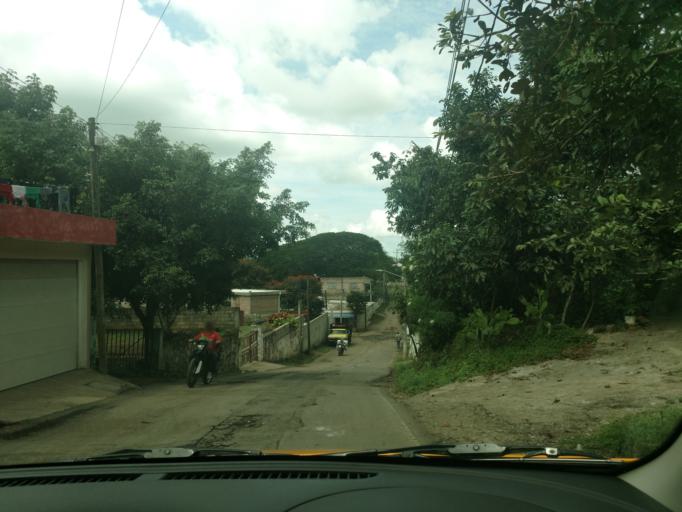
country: MX
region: Nayarit
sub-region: Tepic
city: La Corregidora
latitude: 21.4632
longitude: -104.8004
